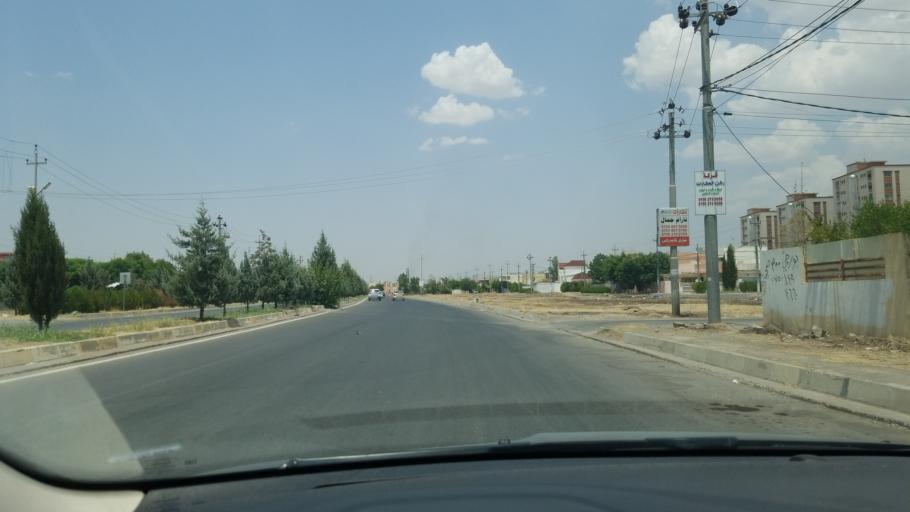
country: IQ
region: Arbil
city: Erbil
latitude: 36.1672
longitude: 44.0586
